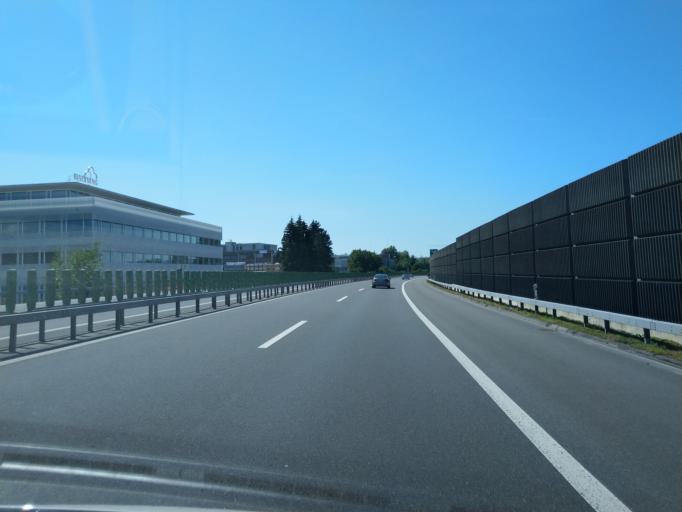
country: CH
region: Zug
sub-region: Zug
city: Steinhausen
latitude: 47.1879
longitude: 8.4899
